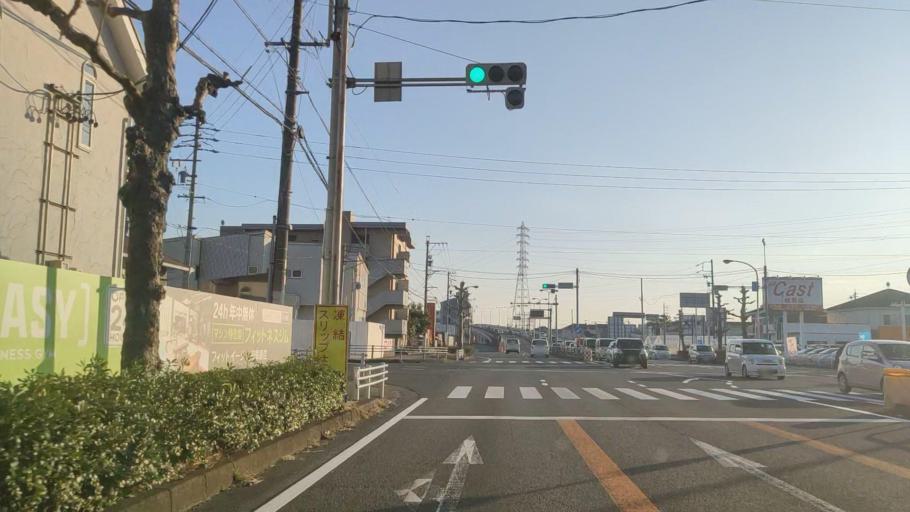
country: JP
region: Gifu
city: Gifu-shi
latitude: 35.4245
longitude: 136.7298
